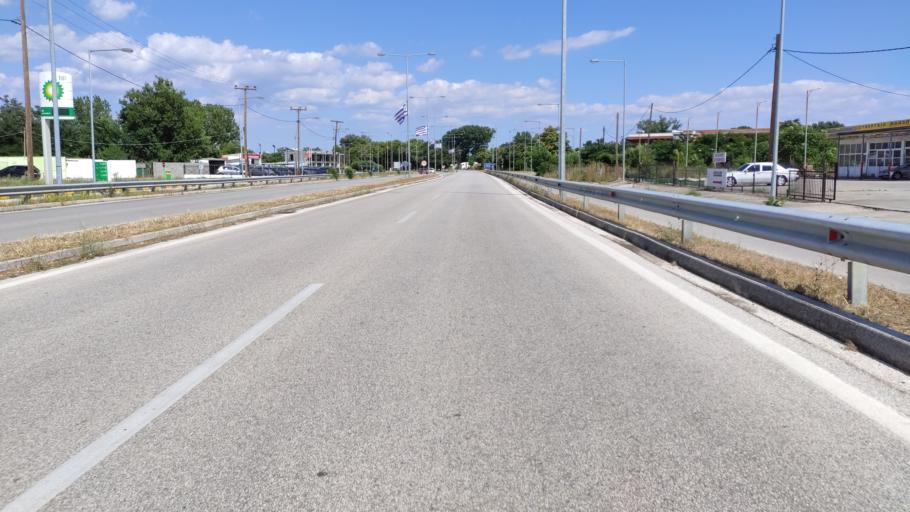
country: GR
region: East Macedonia and Thrace
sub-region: Nomos Rodopis
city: Komotini
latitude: 41.1137
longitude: 25.3838
